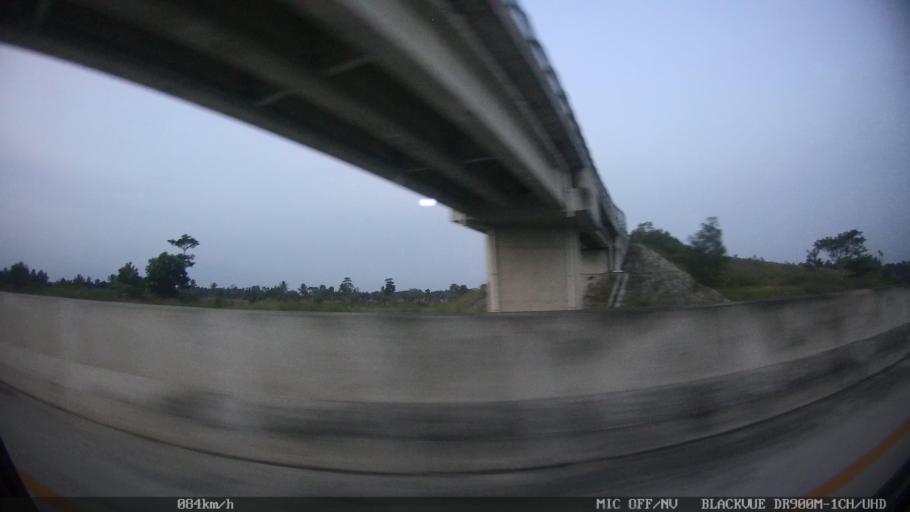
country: ID
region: Lampung
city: Sidorejo
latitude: -5.6427
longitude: 105.5751
